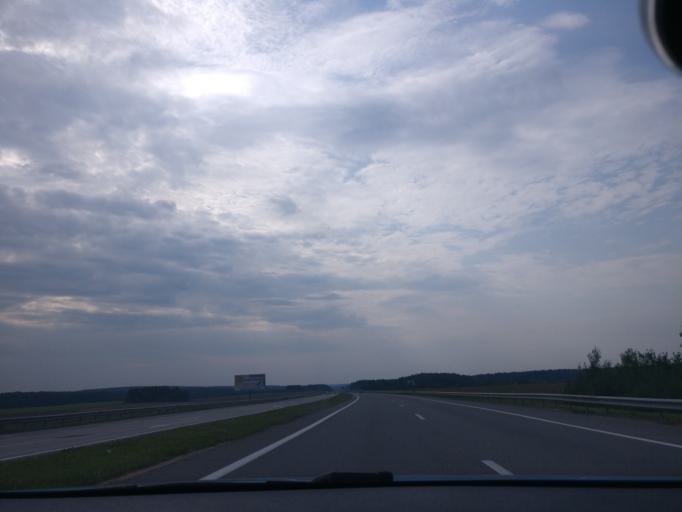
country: BY
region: Minsk
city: Lahoysk
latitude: 54.1530
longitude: 27.8105
